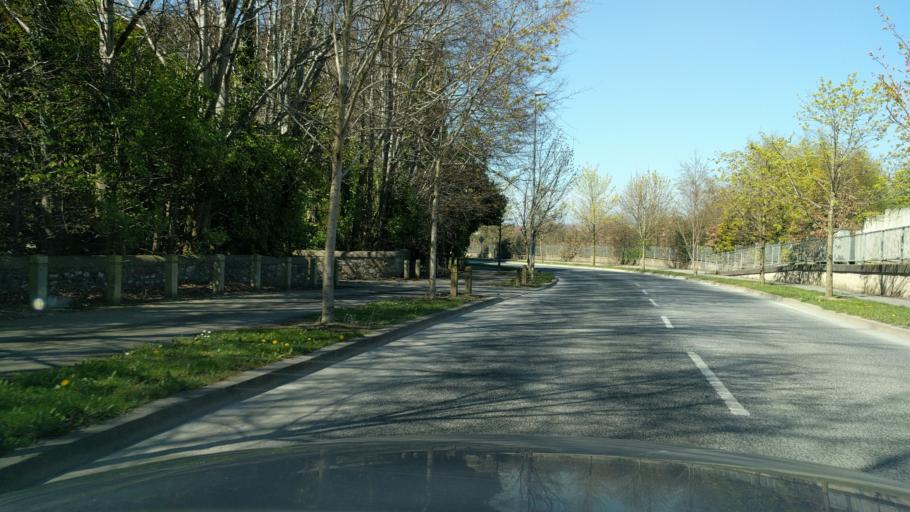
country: IE
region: Leinster
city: Firhouse
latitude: 53.2694
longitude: -6.3392
